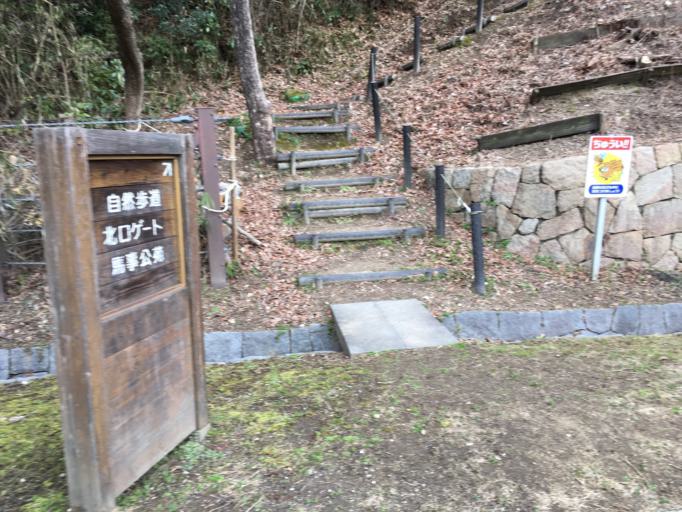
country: JP
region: Hyogo
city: Kobe
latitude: 34.7134
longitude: 135.1121
